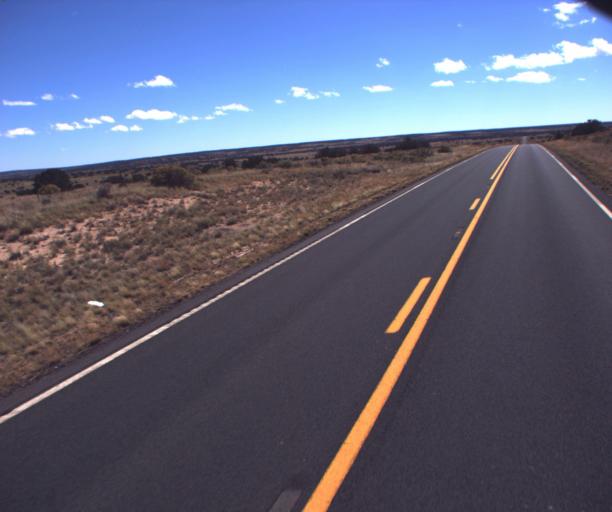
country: US
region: Arizona
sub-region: Apache County
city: Houck
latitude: 35.0225
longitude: -109.2436
